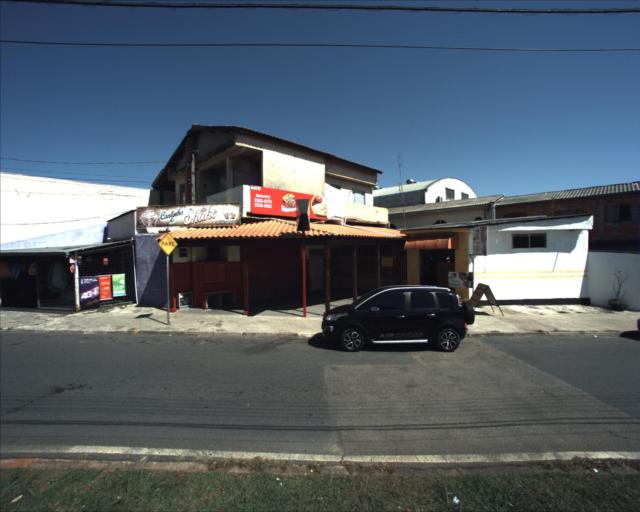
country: BR
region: Sao Paulo
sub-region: Sorocaba
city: Sorocaba
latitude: -23.4697
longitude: -47.4850
